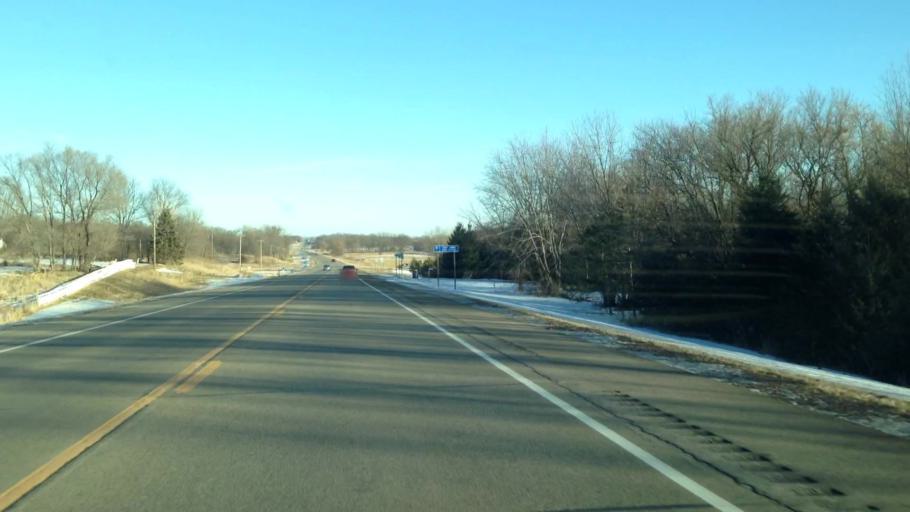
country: US
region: Minnesota
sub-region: Rice County
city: Lonsdale
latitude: 44.4790
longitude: -93.3564
